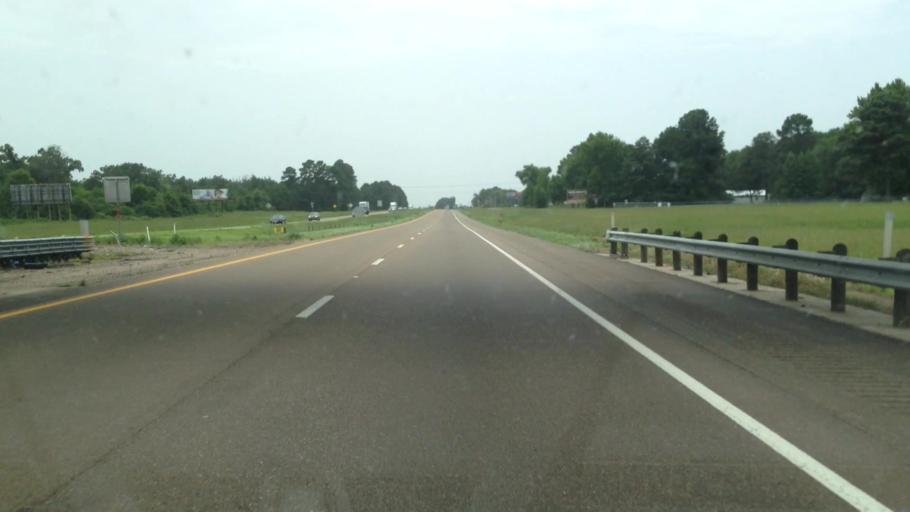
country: US
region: Texas
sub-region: Bowie County
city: New Boston
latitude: 33.4759
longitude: -94.4250
